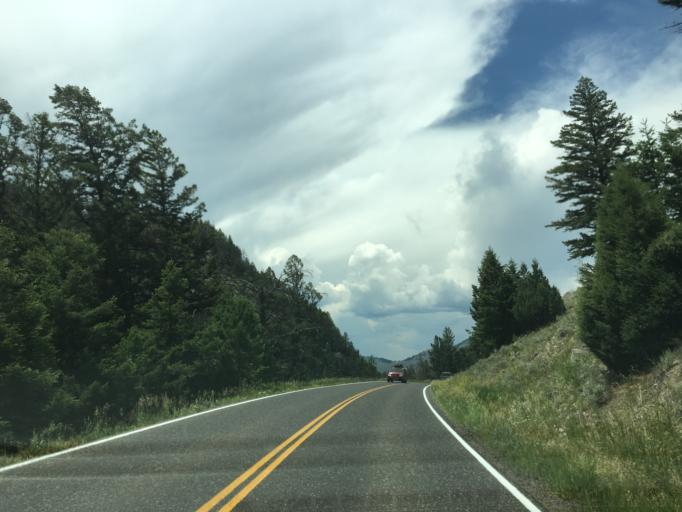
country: US
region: Montana
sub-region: Park County
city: Livingston
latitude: 44.9171
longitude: -110.2904
